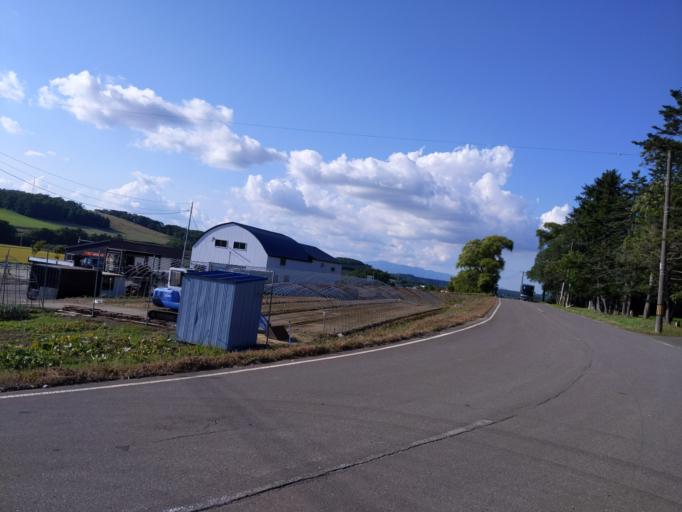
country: JP
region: Hokkaido
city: Iwamizawa
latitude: 43.1992
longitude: 141.8286
